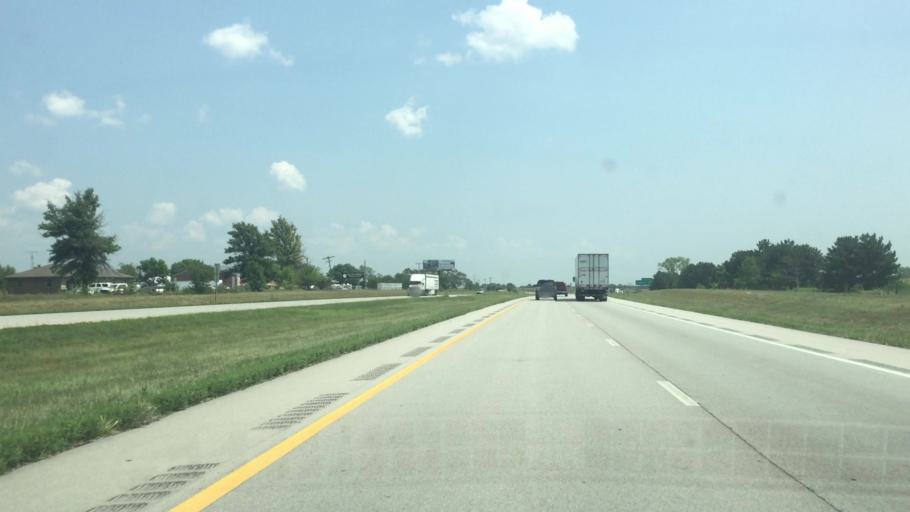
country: US
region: Kansas
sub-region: Johnson County
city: Edgerton
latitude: 38.7431
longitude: -95.0094
